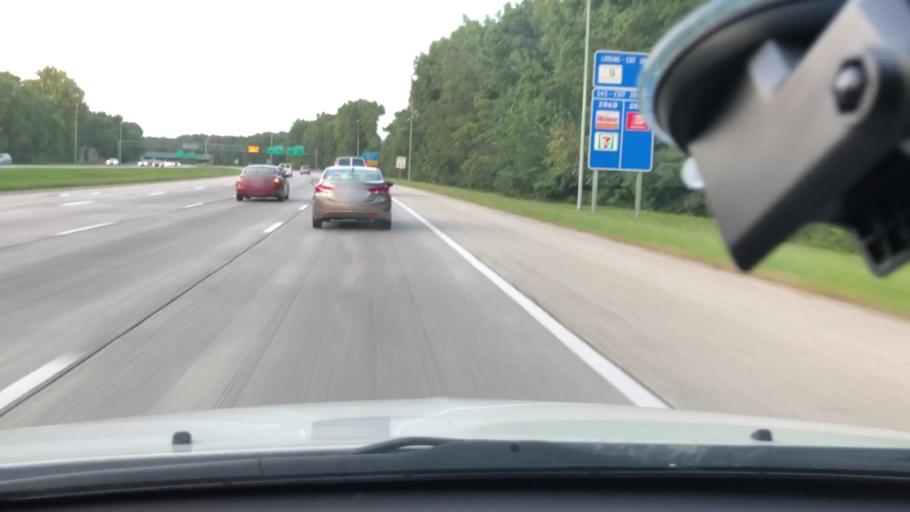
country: US
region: Virginia
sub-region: City of Chesapeake
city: Chesapeake
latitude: 36.8014
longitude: -76.1992
